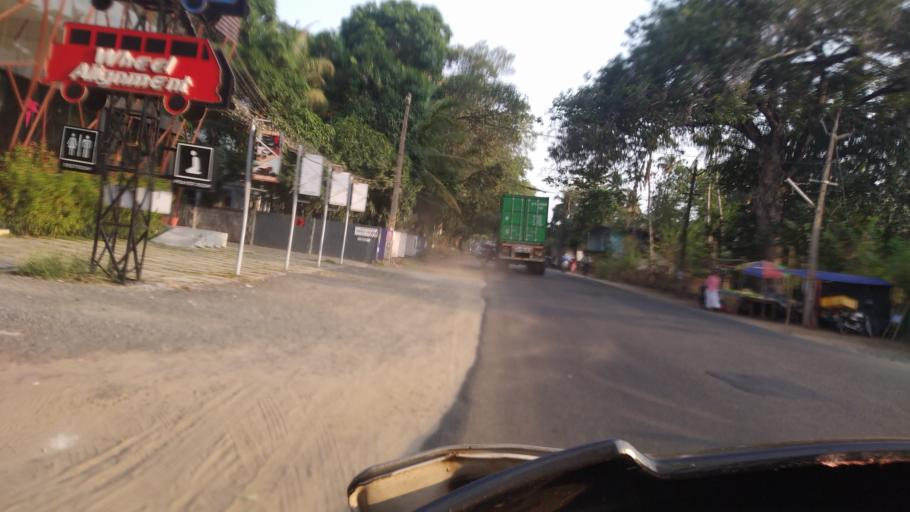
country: IN
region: Kerala
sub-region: Thrissur District
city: Thanniyam
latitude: 10.3600
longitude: 76.1268
